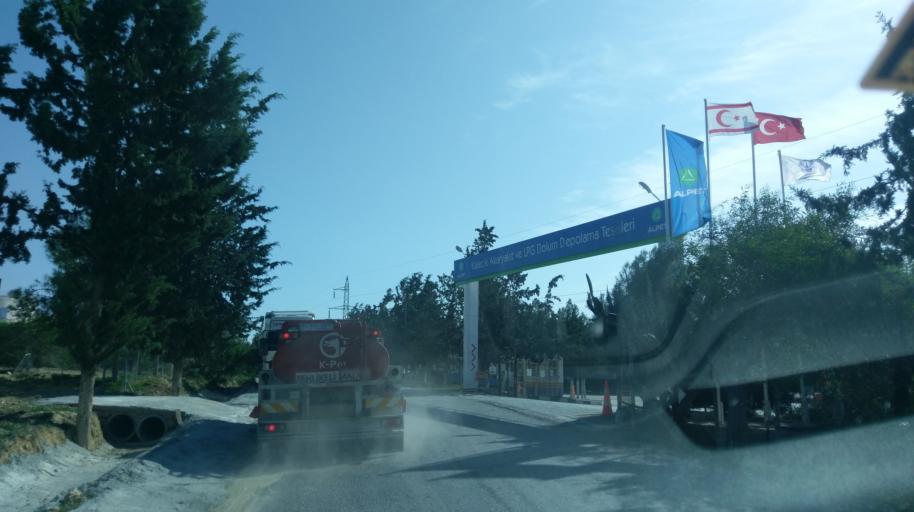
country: CY
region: Ammochostos
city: Trikomo
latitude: 35.3306
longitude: 33.9934
